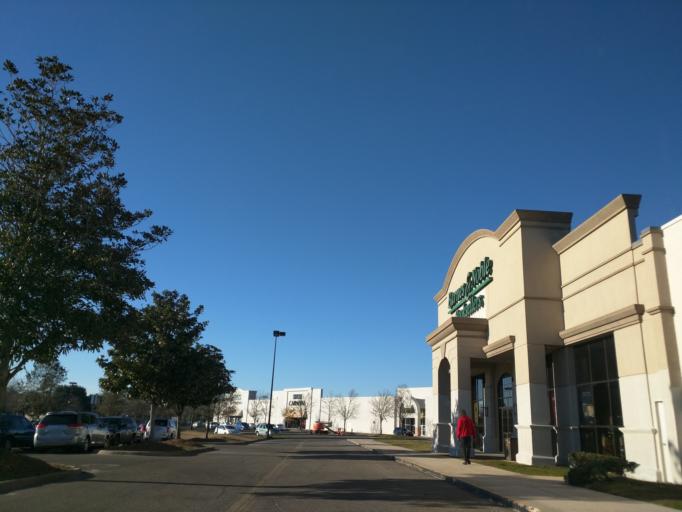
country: US
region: Florida
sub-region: Leon County
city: Tallahassee
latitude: 30.4749
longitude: -84.2920
